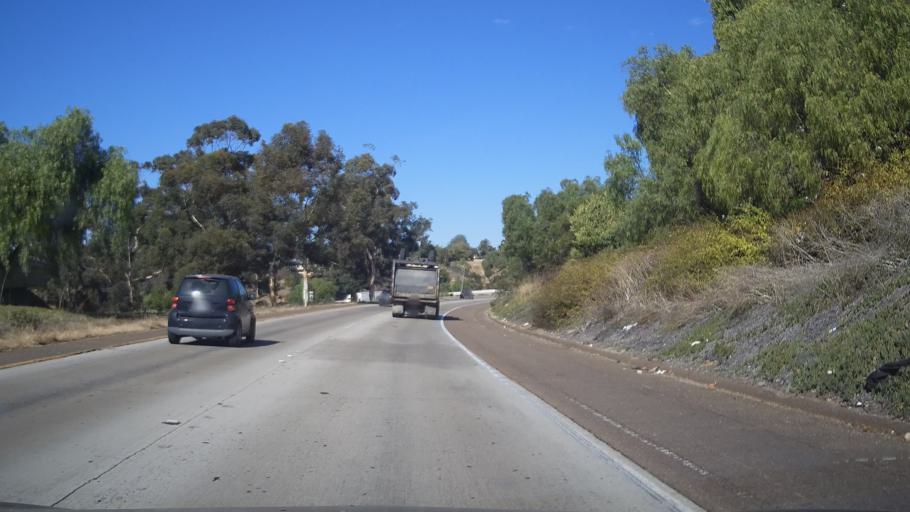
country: US
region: California
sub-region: San Diego County
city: San Diego
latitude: 32.7385
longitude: -117.1127
